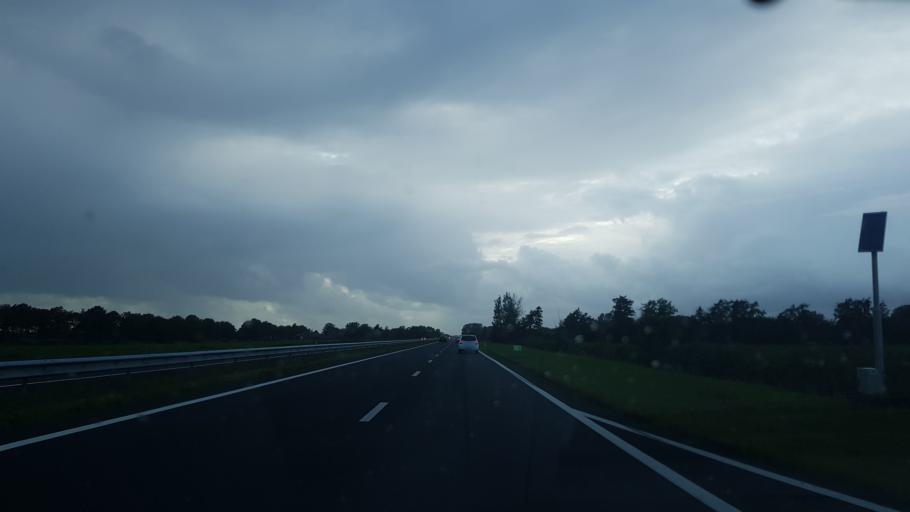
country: NL
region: Friesland
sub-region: Gemeente Tytsjerksteradiel
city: Garyp
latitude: 53.1490
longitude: 5.9844
